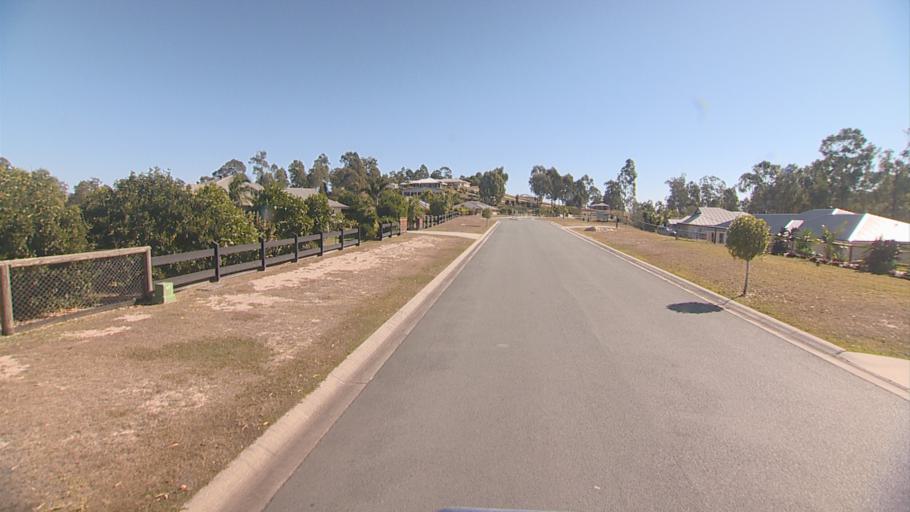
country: AU
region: Queensland
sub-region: Logan
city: Cedar Vale
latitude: -27.8713
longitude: 153.0373
